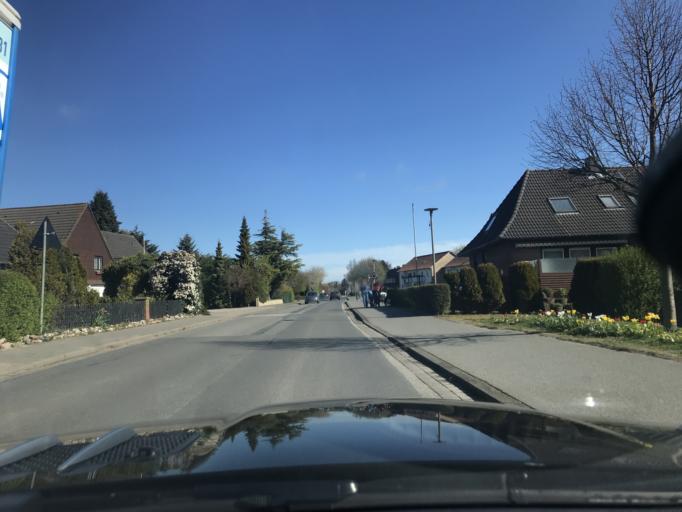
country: DE
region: Schleswig-Holstein
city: Grossenbrode
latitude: 54.3646
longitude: 11.0841
